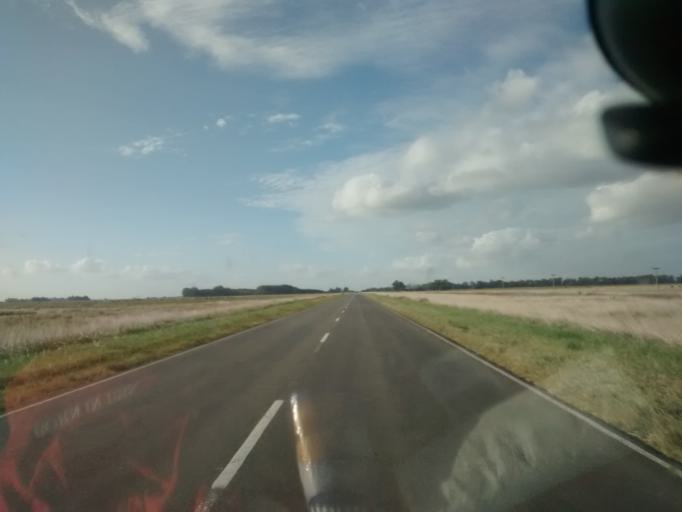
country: AR
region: Buenos Aires
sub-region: Partido de Ayacucho
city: Ayacucho
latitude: -36.6771
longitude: -58.5748
